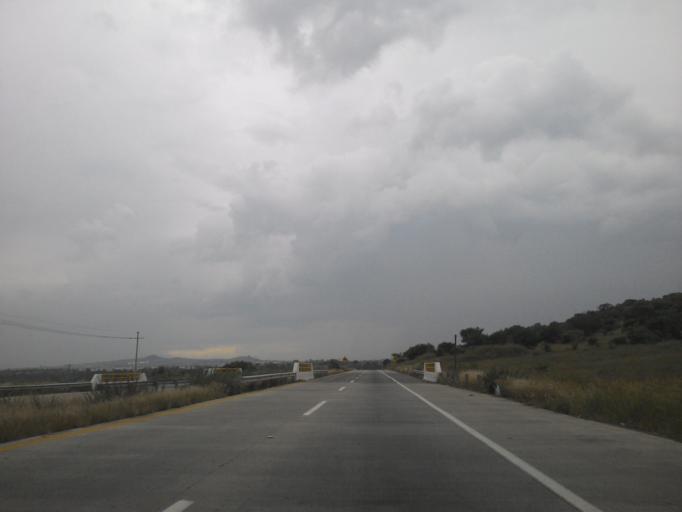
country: MX
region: Jalisco
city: Puente Grande
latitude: 20.5755
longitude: -103.1601
